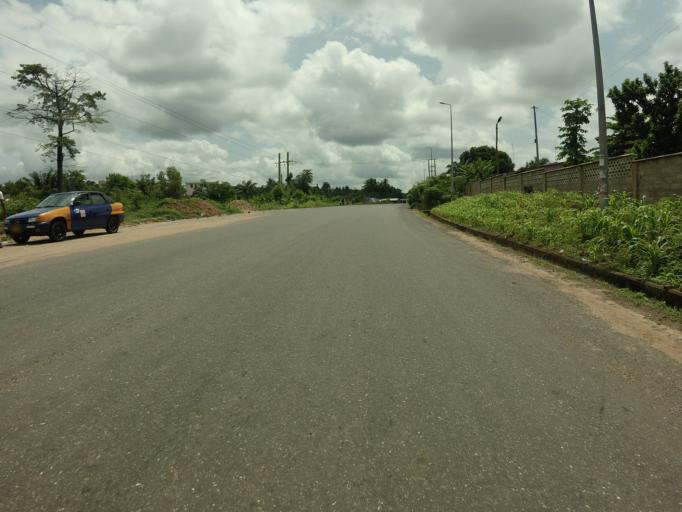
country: GH
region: Volta
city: Ho
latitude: 6.5905
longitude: 0.4730
